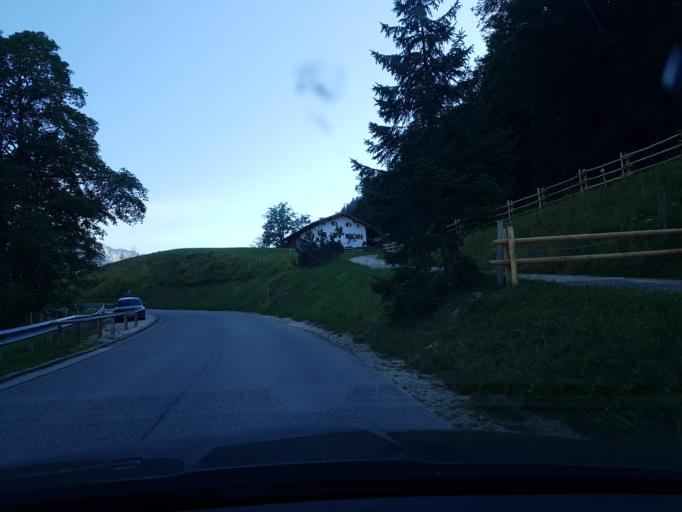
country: DE
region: Bavaria
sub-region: Upper Bavaria
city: Berchtesgaden
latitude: 47.6541
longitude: 13.0028
